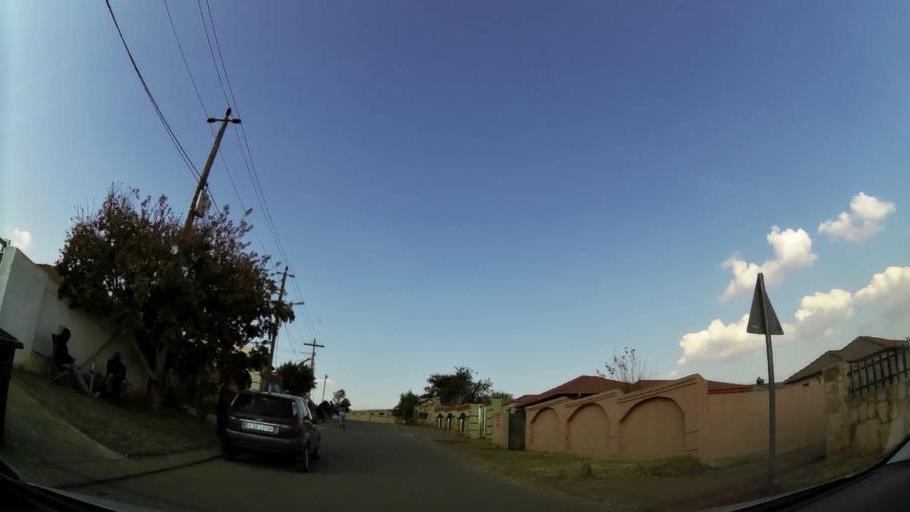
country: ZA
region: Gauteng
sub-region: Ekurhuleni Metropolitan Municipality
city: Tembisa
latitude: -25.9489
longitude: 28.2106
